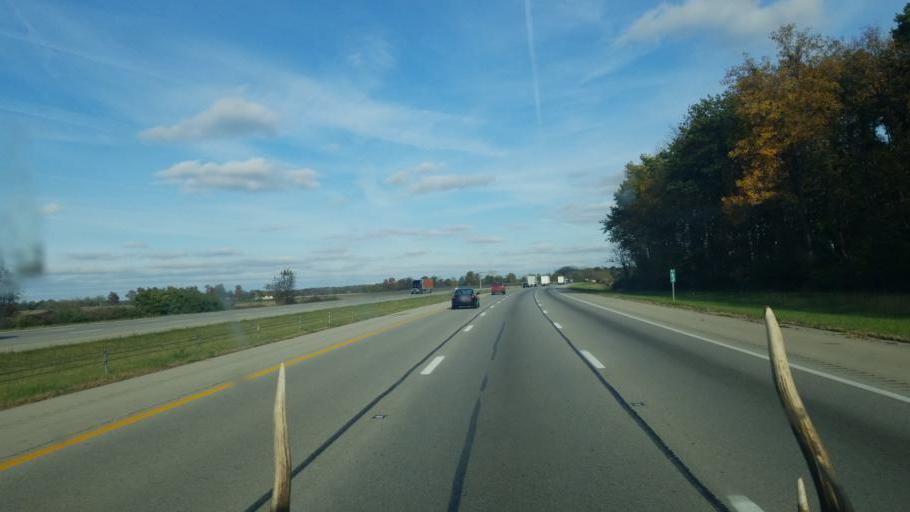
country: US
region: Ohio
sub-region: Clark County
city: Lisbon
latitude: 39.9328
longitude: -83.6745
